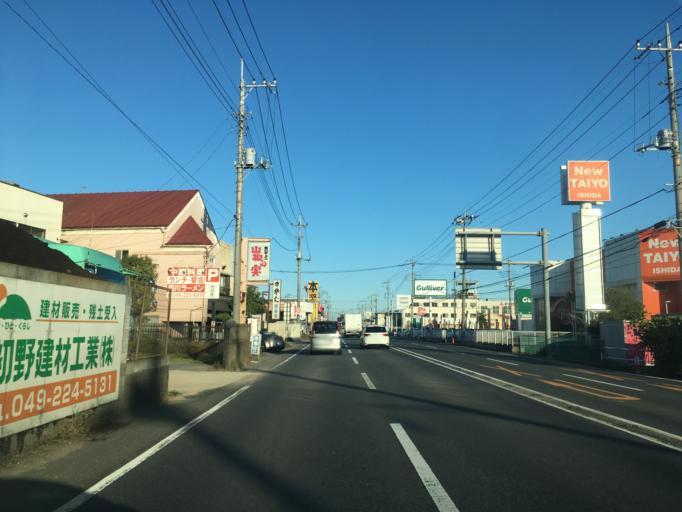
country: JP
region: Saitama
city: Kawagoe
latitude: 35.9362
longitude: 139.4855
